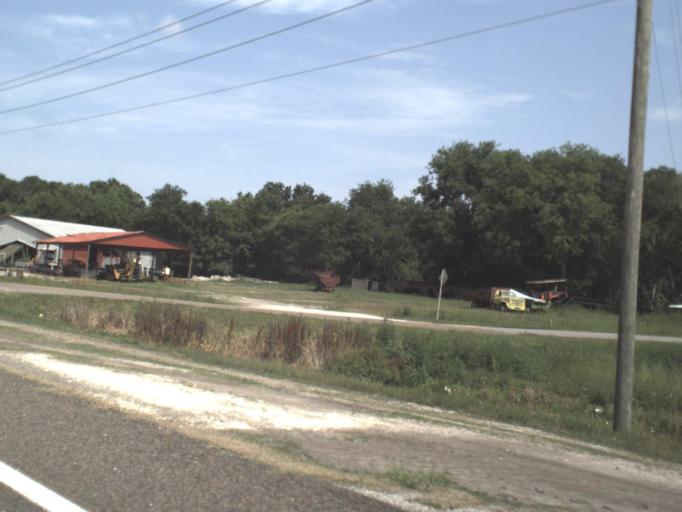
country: US
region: Florida
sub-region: Saint Johns County
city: Saint Augustine Shores
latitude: 29.7770
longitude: -81.4343
